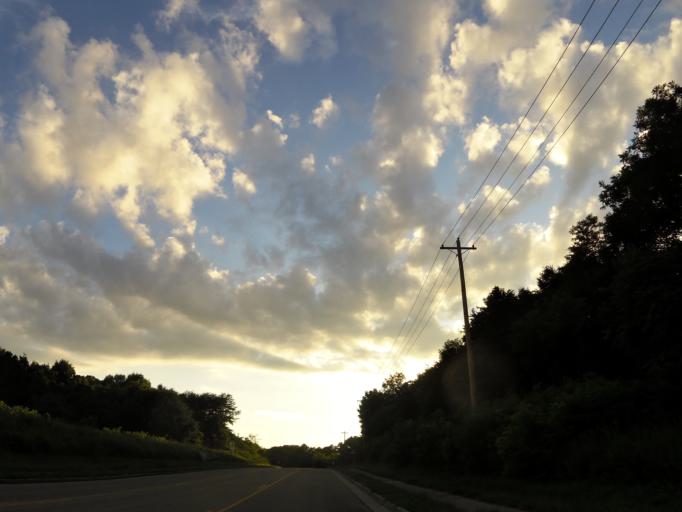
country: US
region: Tennessee
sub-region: Knox County
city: Farragut
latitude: 35.9040
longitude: -84.1624
